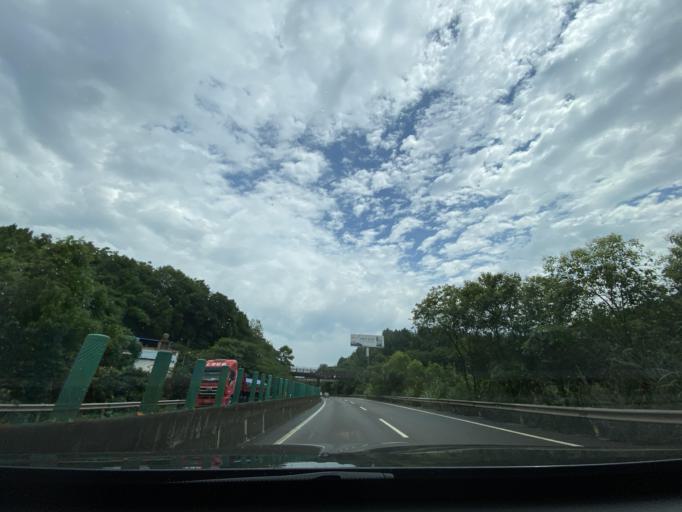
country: CN
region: Sichuan
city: Jiancheng
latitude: 30.2970
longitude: 104.5811
